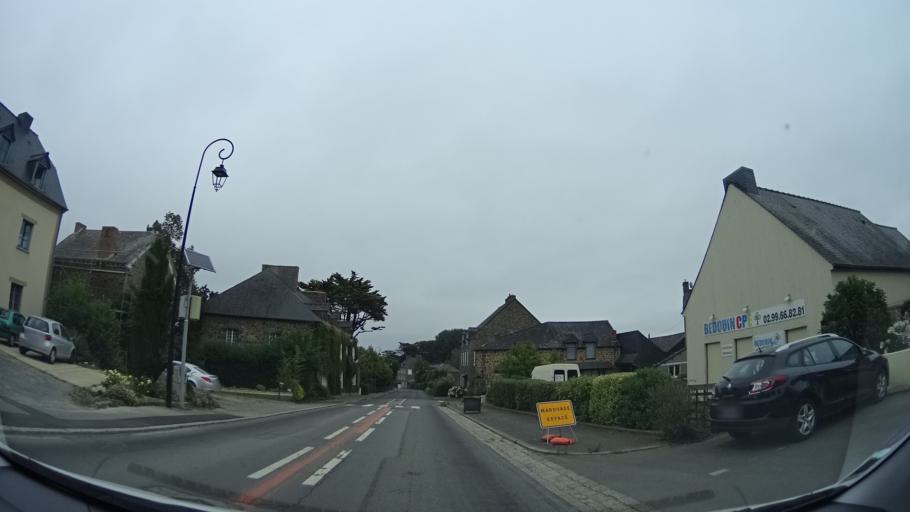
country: FR
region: Brittany
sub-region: Departement d'Ille-et-Vilaine
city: Irodouer
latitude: 48.2973
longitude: -1.9428
